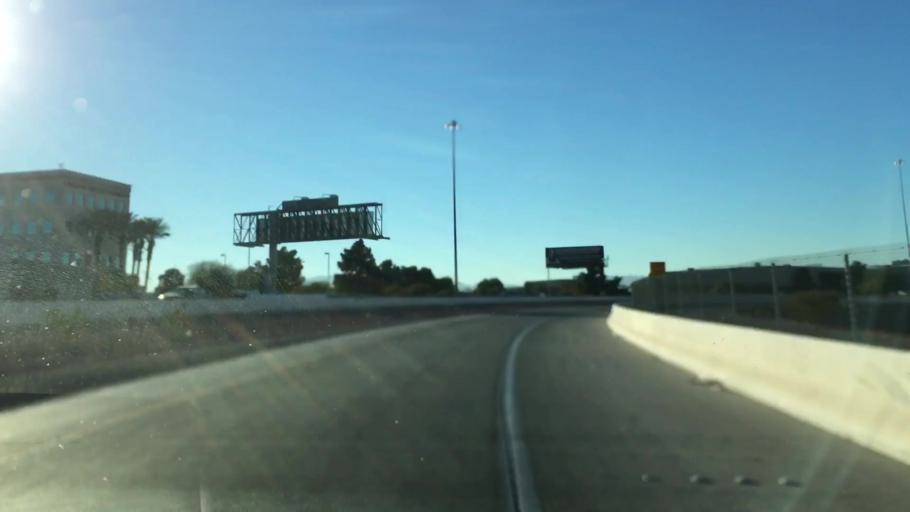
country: US
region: Nevada
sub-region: Clark County
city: Paradise
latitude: 36.0614
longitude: -115.1521
